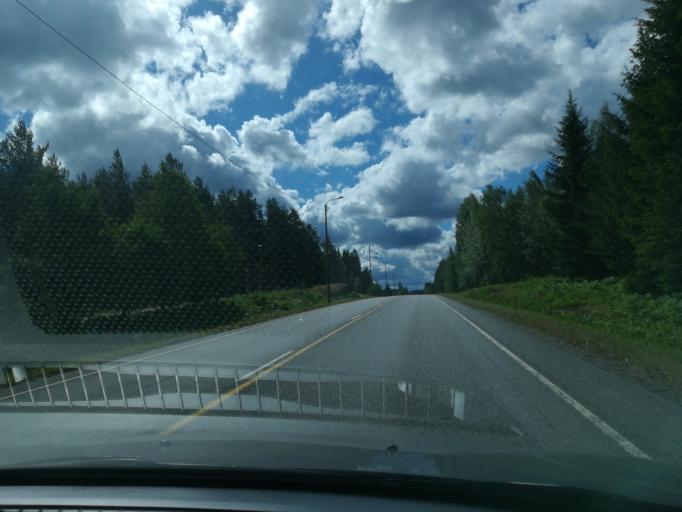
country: FI
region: Southern Savonia
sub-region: Mikkeli
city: Ristiina
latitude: 61.4825
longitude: 27.2502
